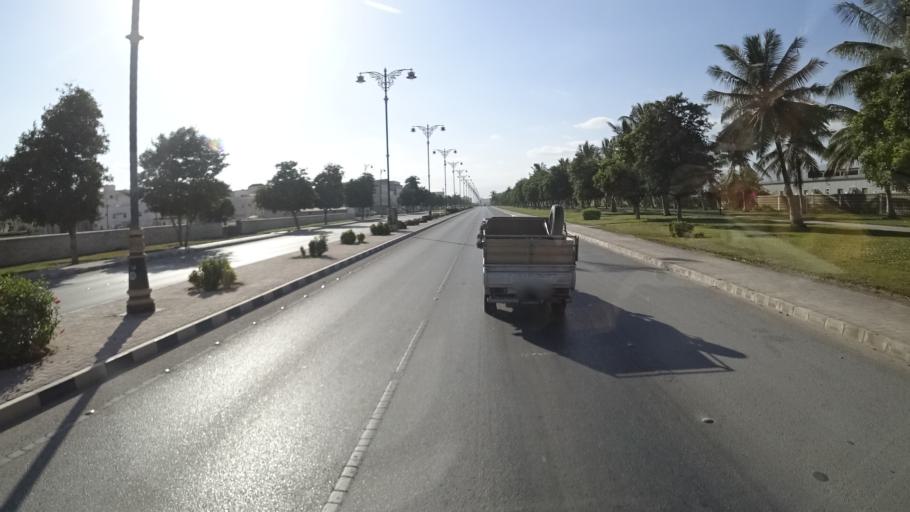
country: OM
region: Zufar
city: Salalah
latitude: 17.0048
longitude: 54.0537
